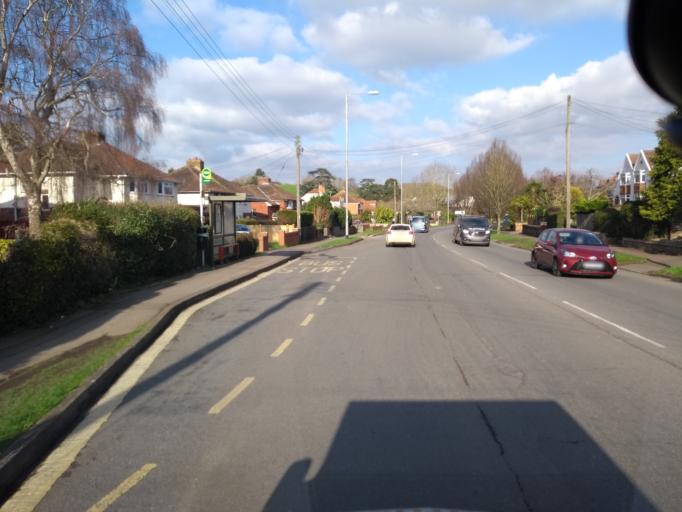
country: GB
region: England
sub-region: Somerset
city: Taunton
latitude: 51.0203
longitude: -3.0733
